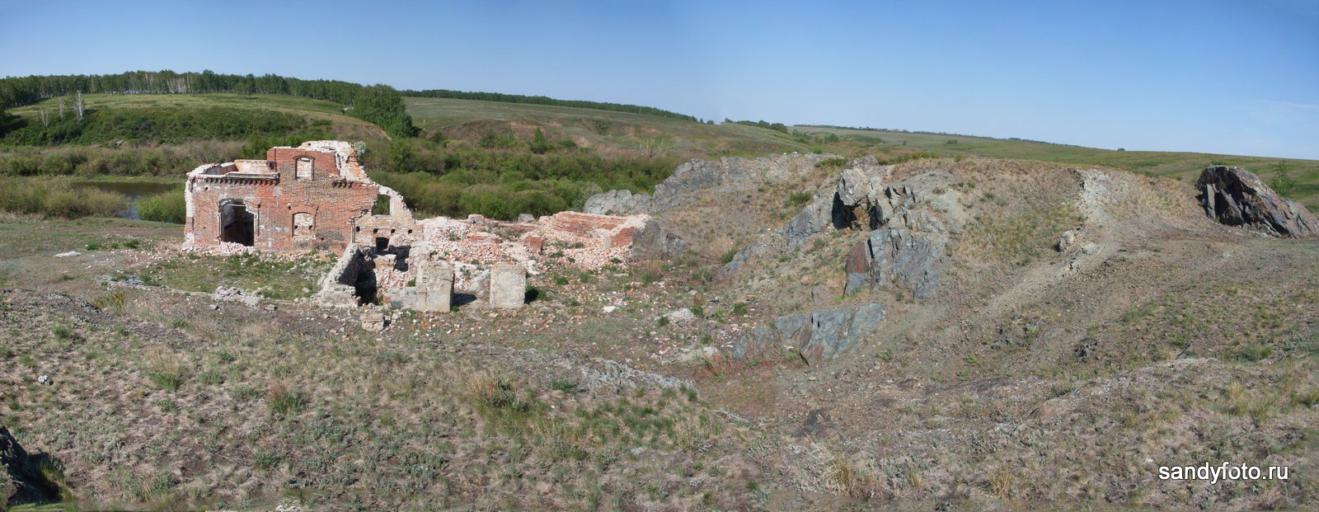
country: RU
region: Chelyabinsk
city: Troitsk
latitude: 54.1352
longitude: 61.4349
